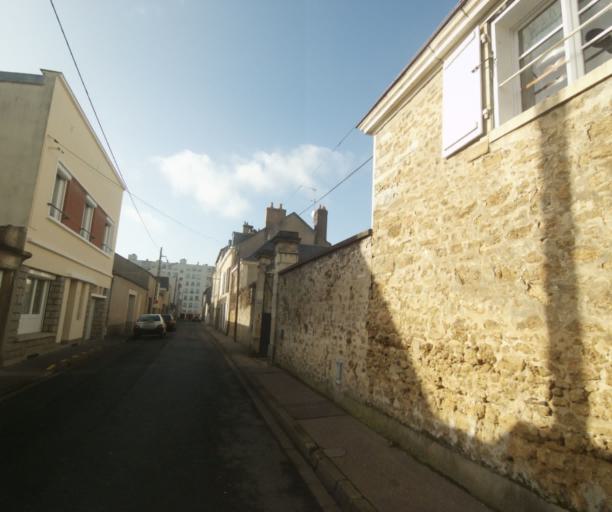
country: FR
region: Pays de la Loire
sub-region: Departement de la Sarthe
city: Le Mans
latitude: 48.0013
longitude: 0.1946
